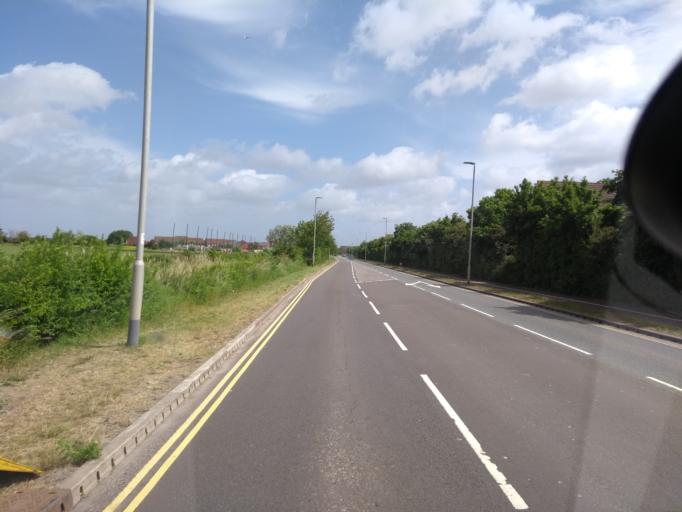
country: GB
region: England
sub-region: Somerset
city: Bridgwater
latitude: 51.1343
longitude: -3.0158
